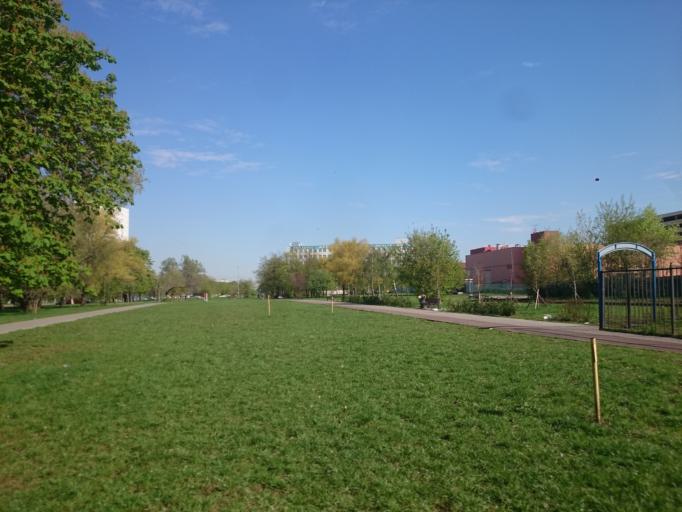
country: RU
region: Moscow
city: Tekstil'shchiki
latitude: 55.7184
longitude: 37.7417
